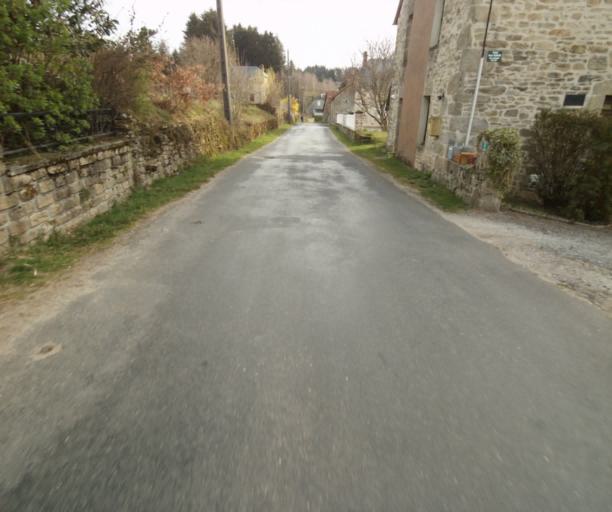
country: FR
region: Limousin
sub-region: Departement de la Correze
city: Treignac
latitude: 45.4745
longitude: 1.7883
